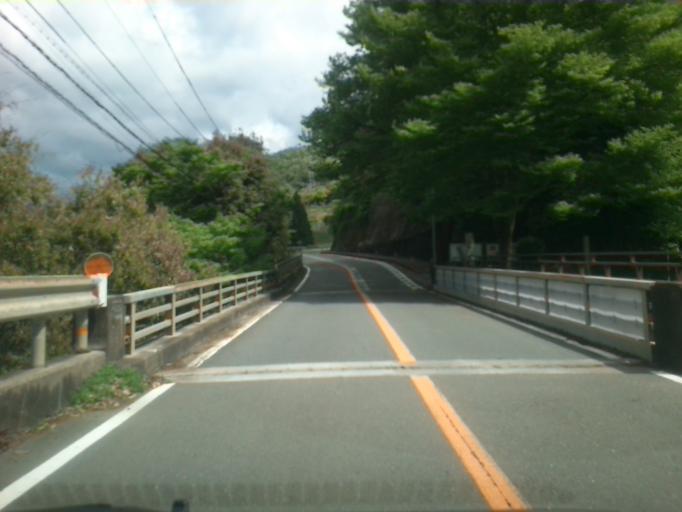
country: JP
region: Kyoto
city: Ayabe
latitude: 35.2186
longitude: 135.4198
